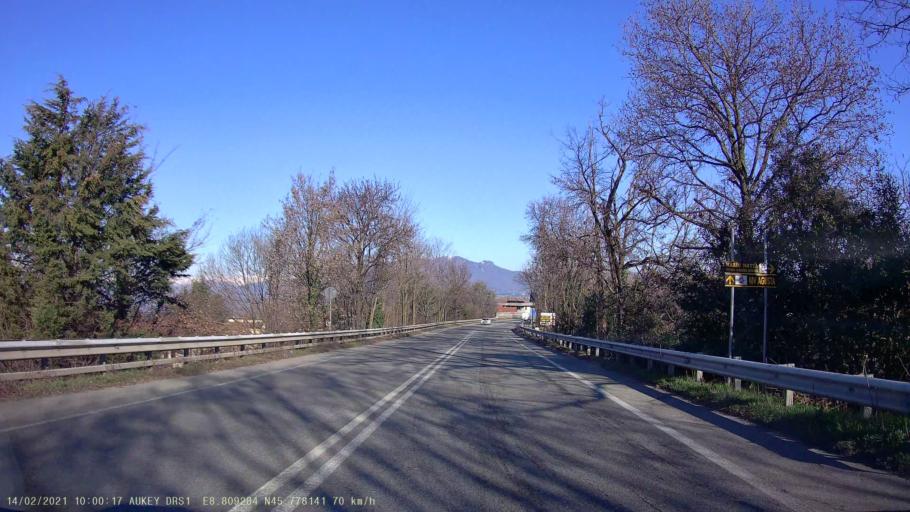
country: IT
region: Lombardy
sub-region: Provincia di Varese
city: Buguggiate
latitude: 45.7785
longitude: 8.8092
